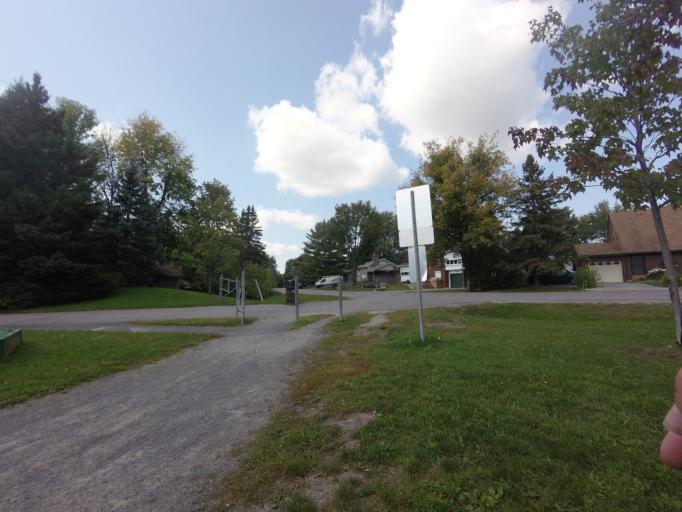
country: CA
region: Ontario
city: Bells Corners
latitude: 45.2348
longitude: -75.6965
